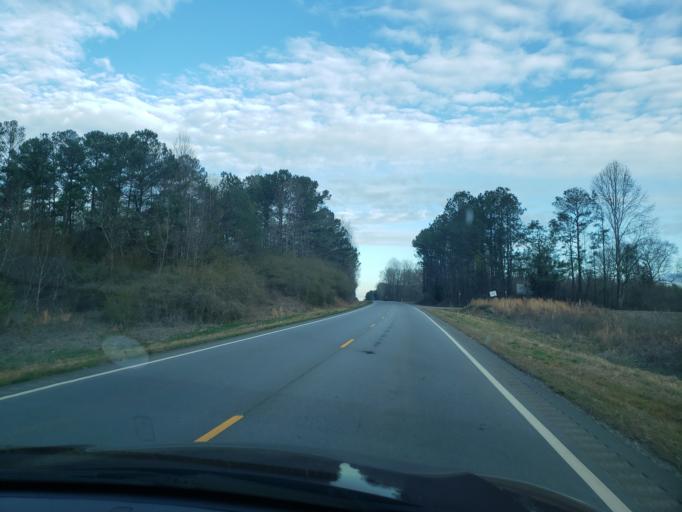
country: US
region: Alabama
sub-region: Randolph County
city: Wedowee
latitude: 33.2631
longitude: -85.4562
